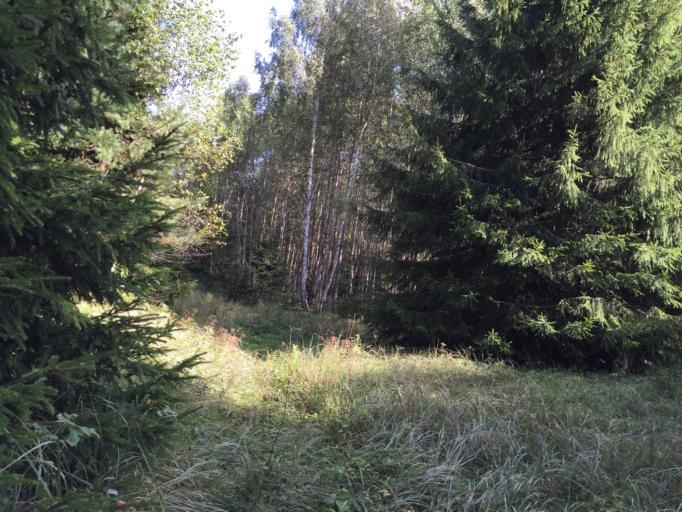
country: LV
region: Kuldigas Rajons
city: Kuldiga
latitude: 57.0058
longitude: 21.7821
